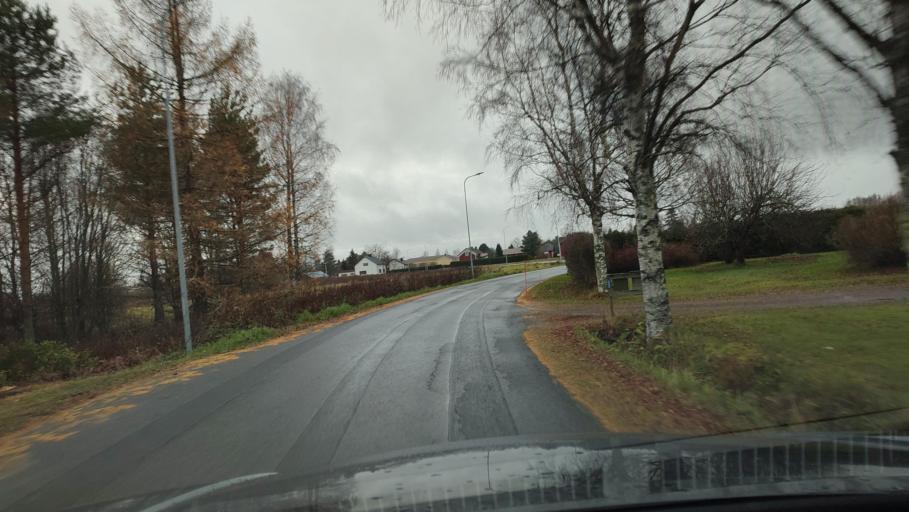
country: FI
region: Ostrobothnia
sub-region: Sydosterbotten
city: Kristinestad
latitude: 62.2540
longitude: 21.5380
